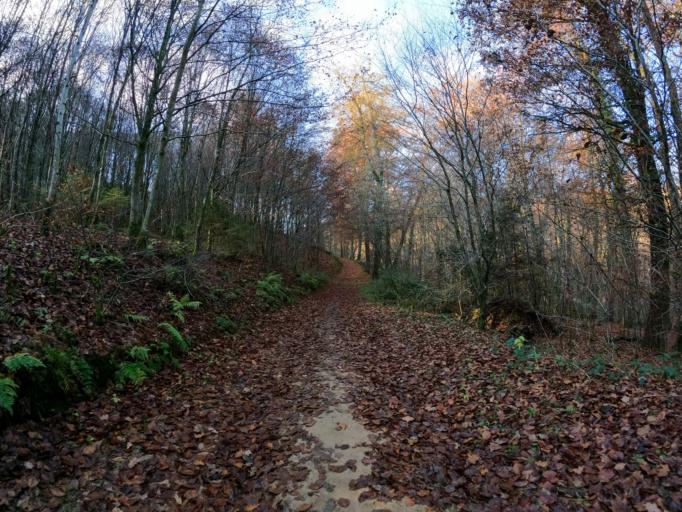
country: LU
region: Luxembourg
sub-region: Canton de Capellen
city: Mamer
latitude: 49.6437
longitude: 6.0329
